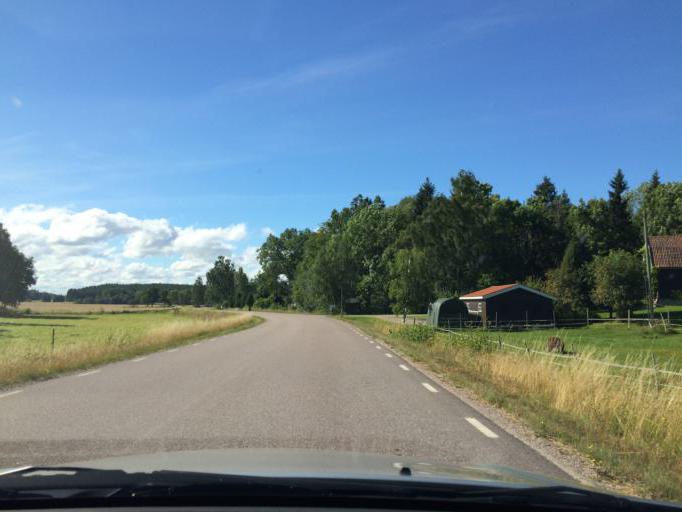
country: SE
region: Soedermanland
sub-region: Eskilstuna Kommun
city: Torshalla
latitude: 59.5177
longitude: 16.4369
